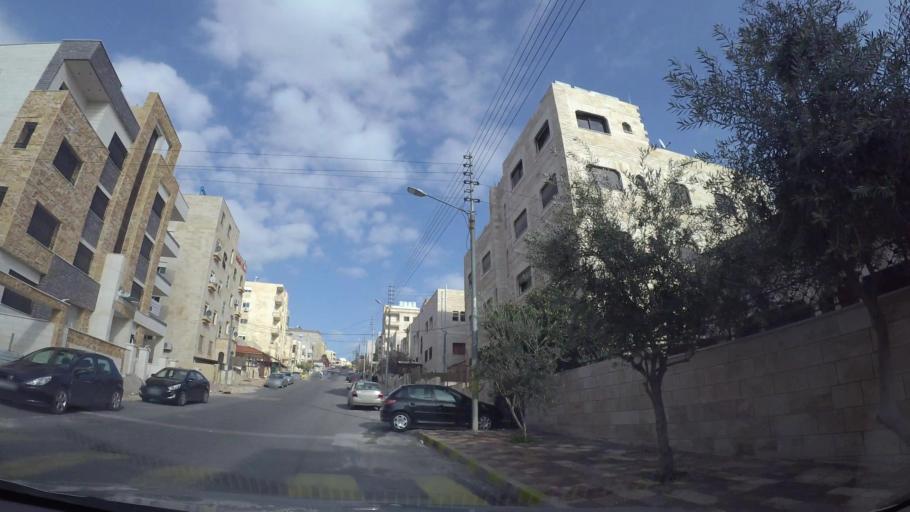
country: JO
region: Amman
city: Al Jubayhah
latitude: 32.0196
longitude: 35.8517
